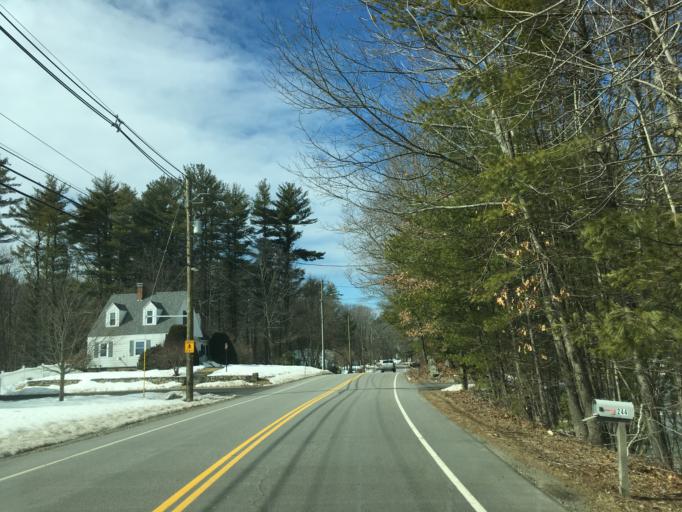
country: US
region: New Hampshire
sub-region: Rockingham County
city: North Hampton
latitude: 42.9746
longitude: -70.8374
